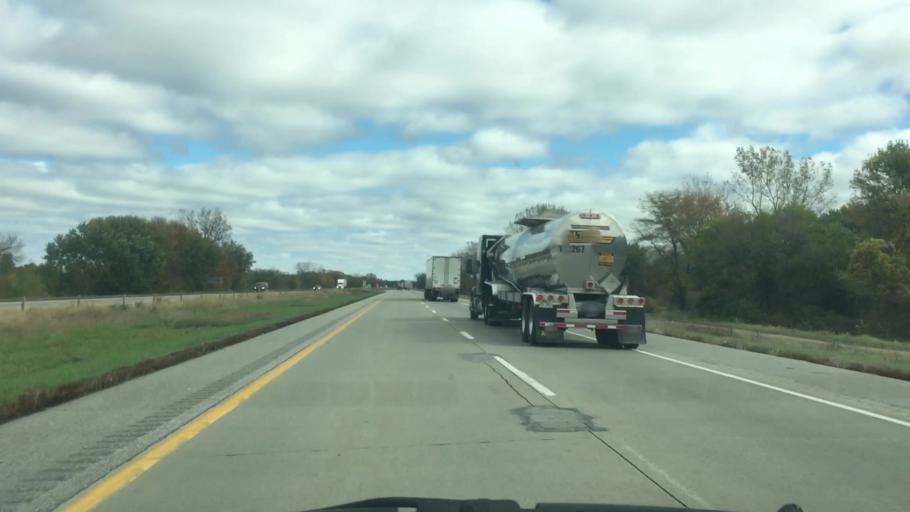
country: US
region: Iowa
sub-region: Jasper County
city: Colfax
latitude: 41.6952
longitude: -93.2319
